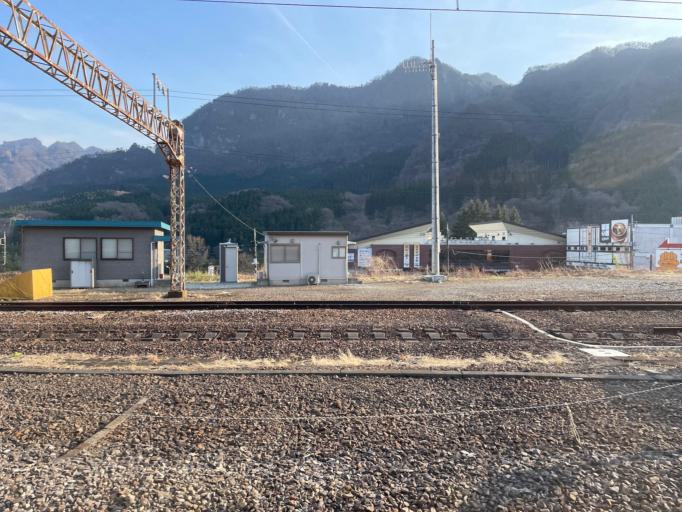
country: JP
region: Gunma
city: Annaka
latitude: 36.3359
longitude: 138.7395
